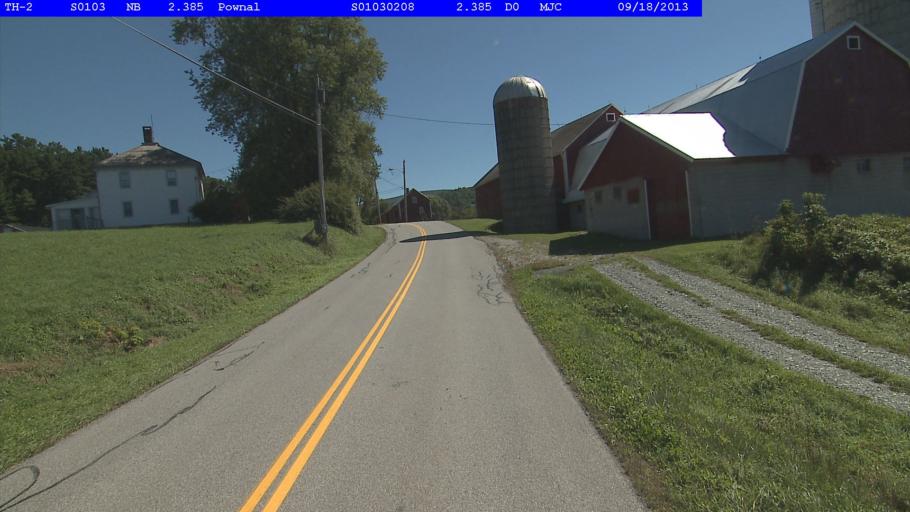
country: US
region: Vermont
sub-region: Bennington County
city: Bennington
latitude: 42.7977
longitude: -73.2314
